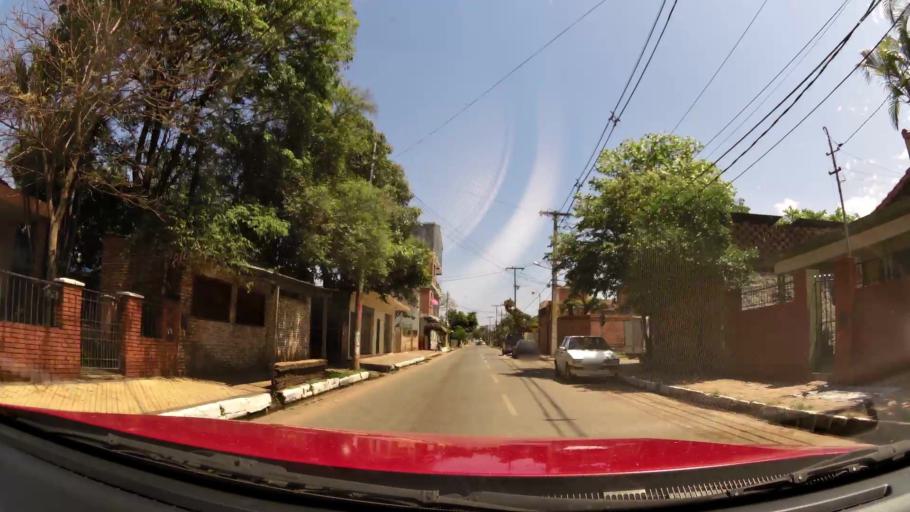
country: PY
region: Central
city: Fernando de la Mora
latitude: -25.3259
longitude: -57.5561
